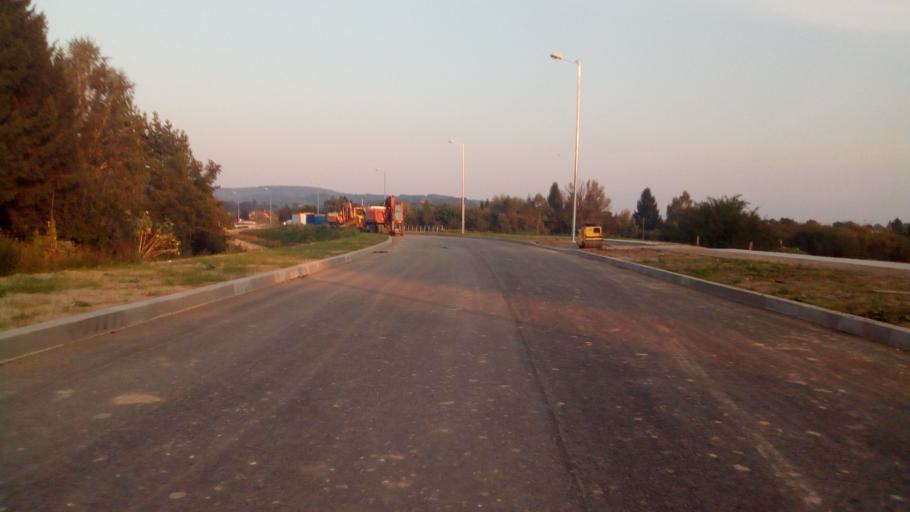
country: PL
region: Subcarpathian Voivodeship
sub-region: Powiat strzyzowski
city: Strzyzow
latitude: 49.8670
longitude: 21.7823
